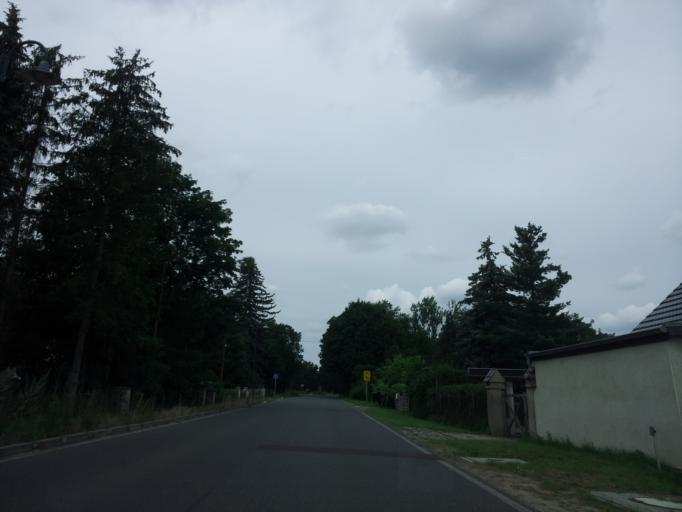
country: DE
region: Brandenburg
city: Trebbin
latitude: 52.2216
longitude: 13.1984
